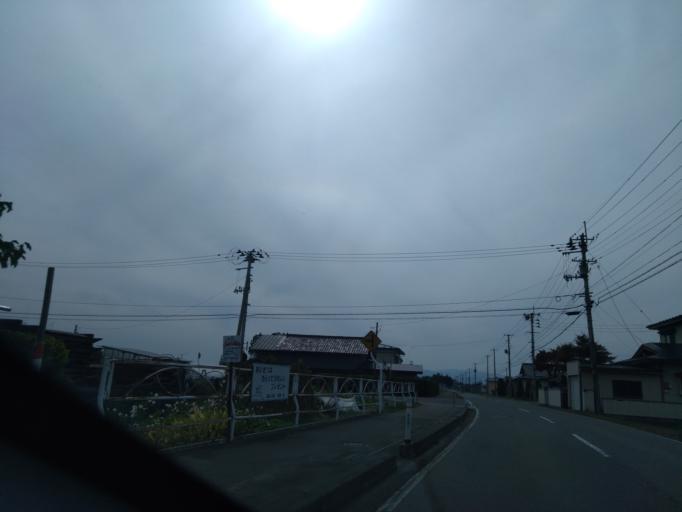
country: JP
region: Iwate
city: Hanamaki
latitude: 39.4442
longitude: 141.0854
